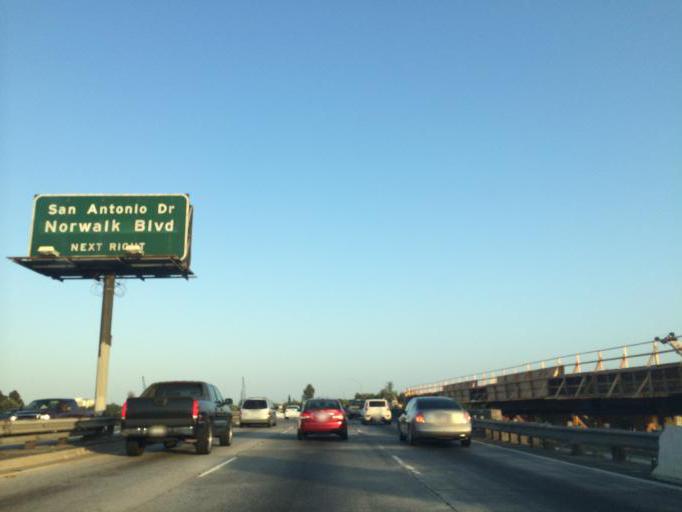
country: US
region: California
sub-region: Los Angeles County
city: Norwalk
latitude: 33.9177
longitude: -118.0803
